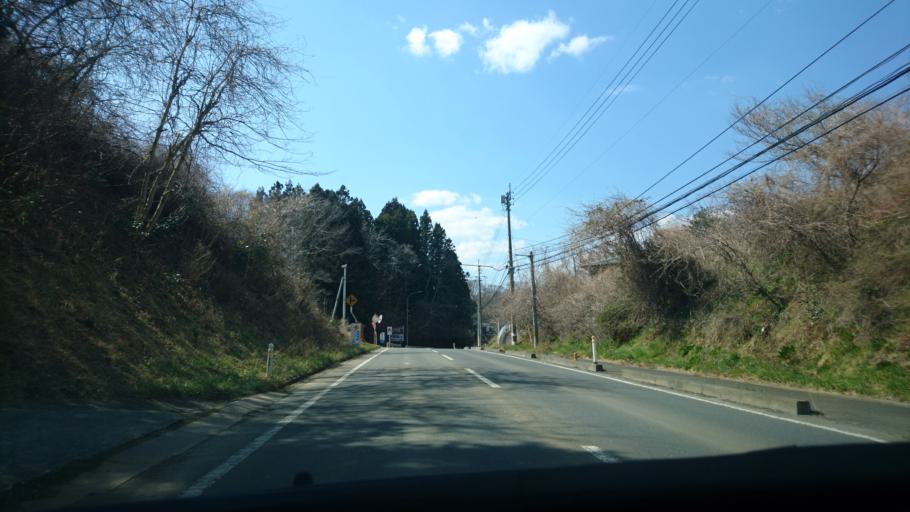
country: JP
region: Miyagi
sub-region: Oshika Gun
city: Onagawa Cho
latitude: 38.6412
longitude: 141.4825
